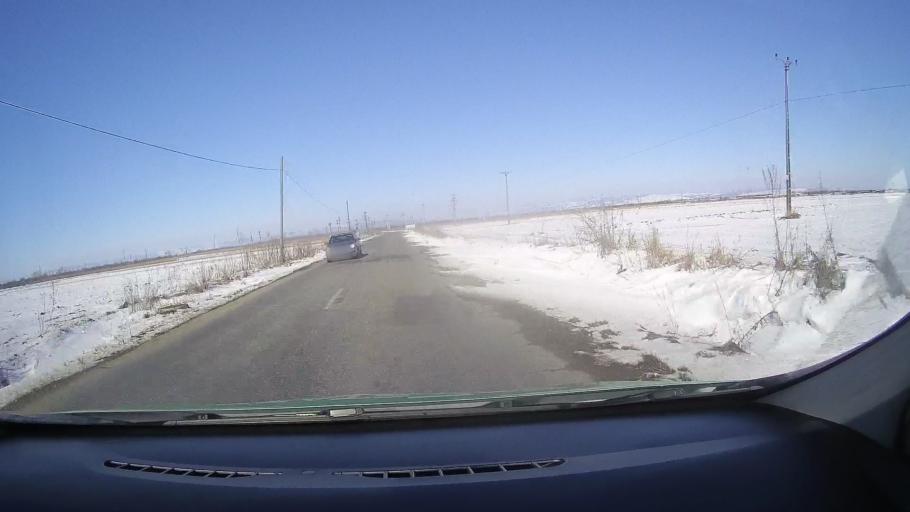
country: RO
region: Brasov
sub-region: Comuna Harseni
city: Harseni
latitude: 45.7610
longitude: 25.0079
